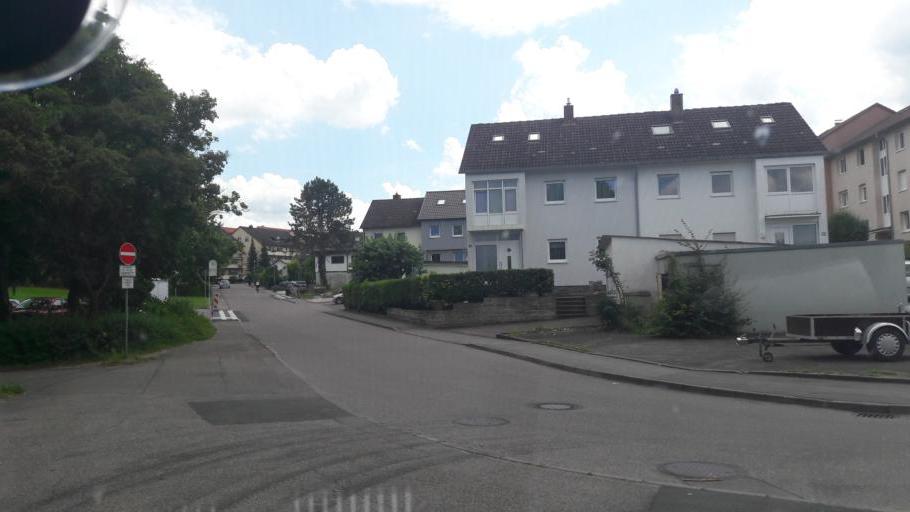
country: DE
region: Baden-Wuerttemberg
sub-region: Regierungsbezirk Stuttgart
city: Ohringen
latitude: 49.1955
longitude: 9.5124
